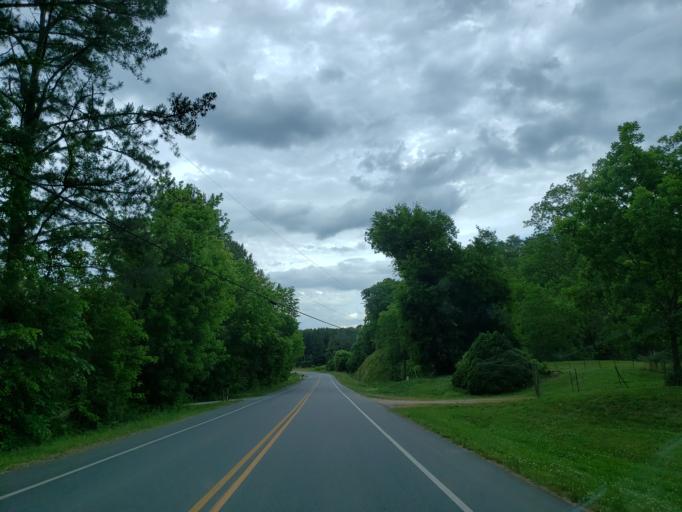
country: US
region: Georgia
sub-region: Polk County
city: Rockmart
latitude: 33.9786
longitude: -85.0436
